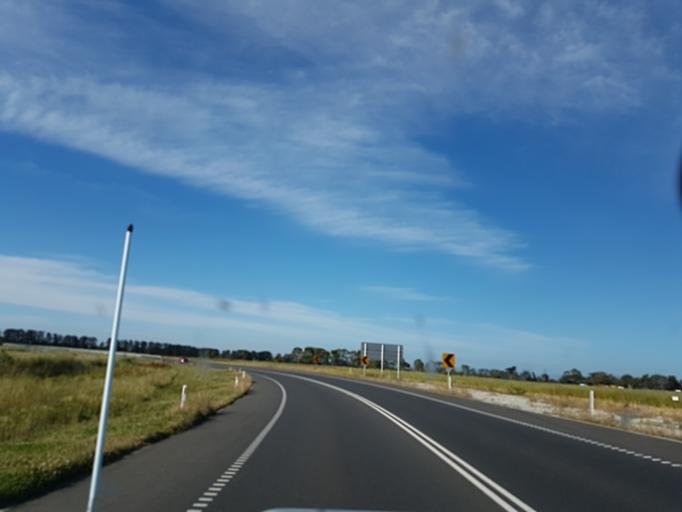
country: AU
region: Victoria
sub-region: Cardinia
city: Koo-Wee-Rup
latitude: -38.2070
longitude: 145.4735
